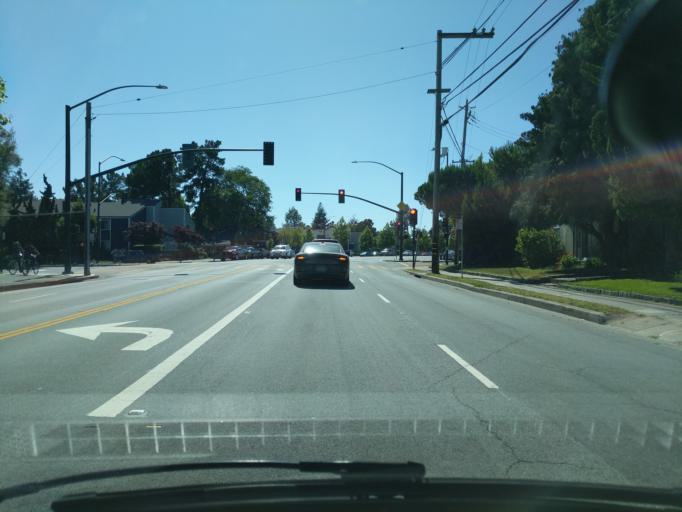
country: US
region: California
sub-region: Alameda County
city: Oakland
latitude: 37.7717
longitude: -122.2855
